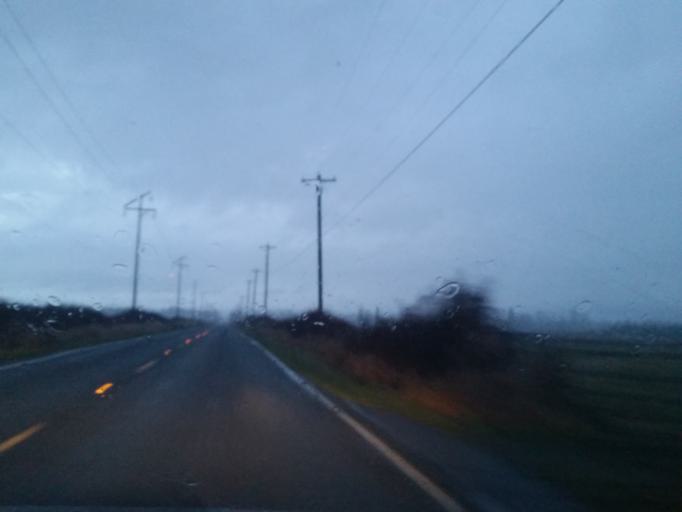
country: US
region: Washington
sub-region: Snohomish County
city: Everett
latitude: 47.9547
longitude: -122.1739
